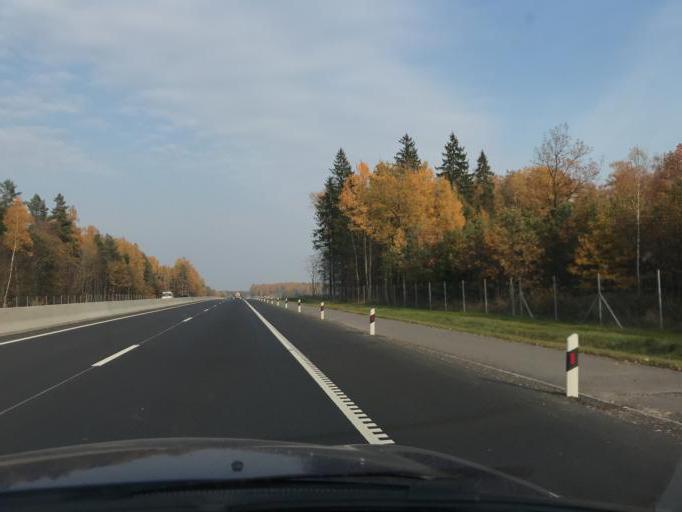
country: BY
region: Grodnenskaya
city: Shchuchin
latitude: 53.6730
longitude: 24.8341
